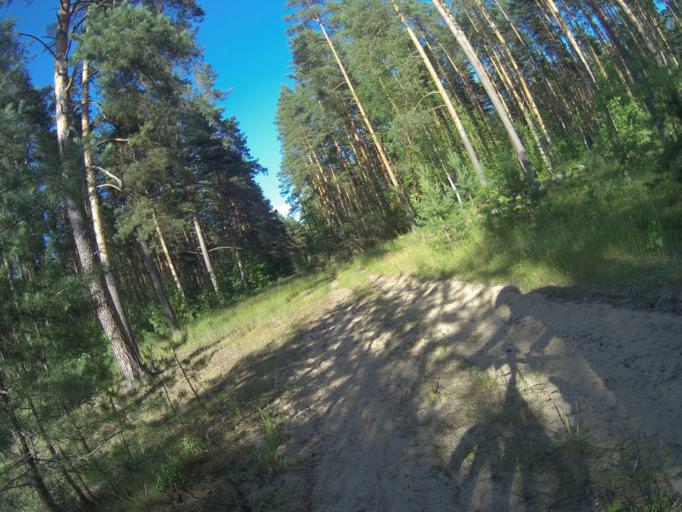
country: RU
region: Vladimir
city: Bogolyubovo
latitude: 56.1248
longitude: 40.5161
